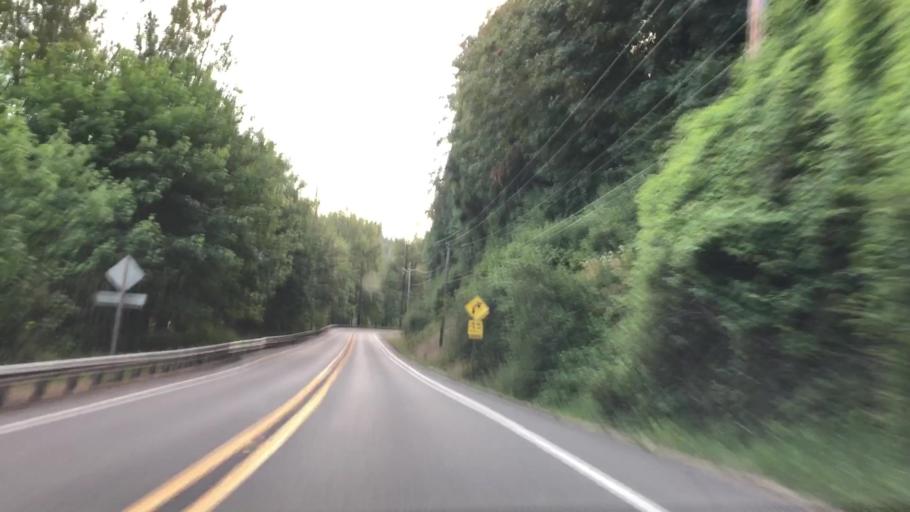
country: US
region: Washington
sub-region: King County
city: Ames Lake
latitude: 47.6282
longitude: -121.9889
